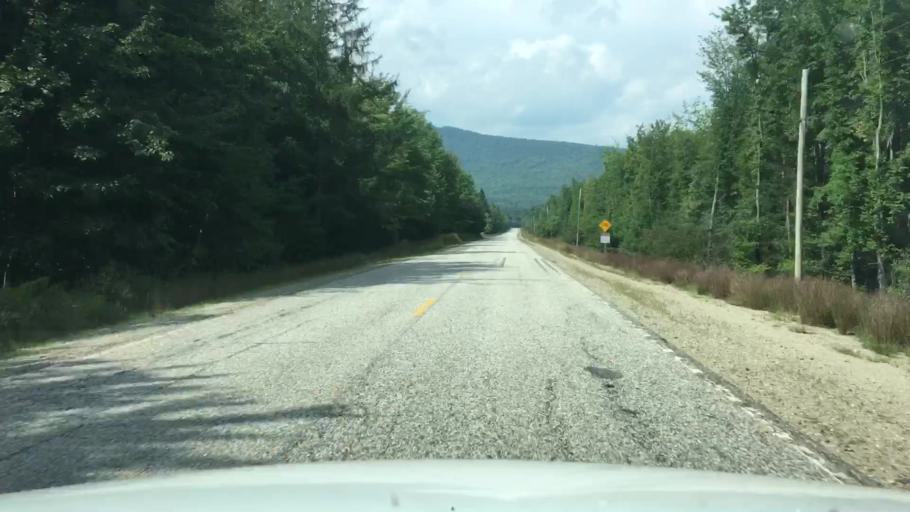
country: US
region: Maine
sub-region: Oxford County
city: Rumford
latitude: 44.5719
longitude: -70.7216
